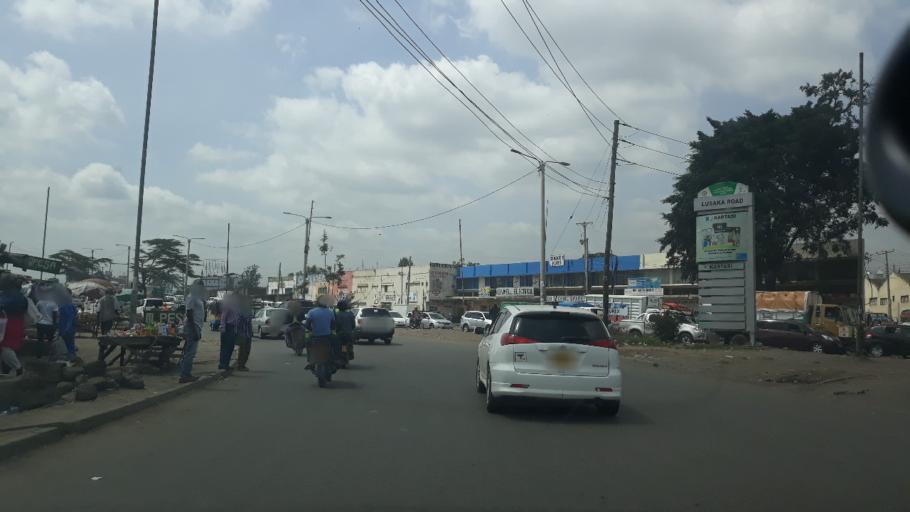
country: KE
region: Nairobi Area
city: Pumwani
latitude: -1.2924
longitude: 36.8411
